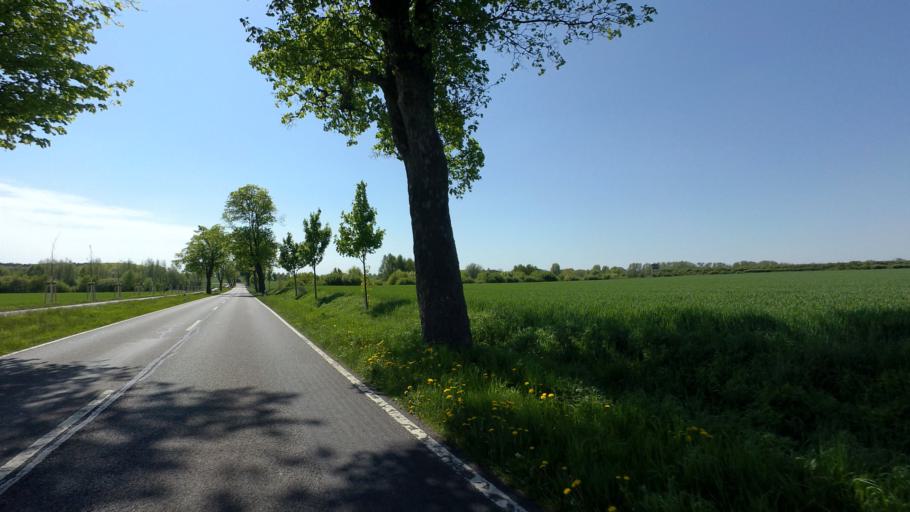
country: DE
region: Brandenburg
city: Schulzendorf
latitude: 52.3533
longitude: 13.5576
